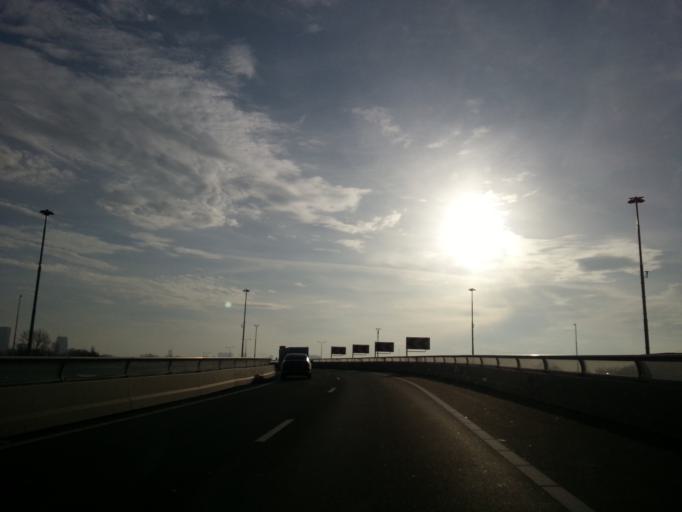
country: NL
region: South Holland
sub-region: Gemeente Rotterdam
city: Delfshaven
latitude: 51.9323
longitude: 4.4375
